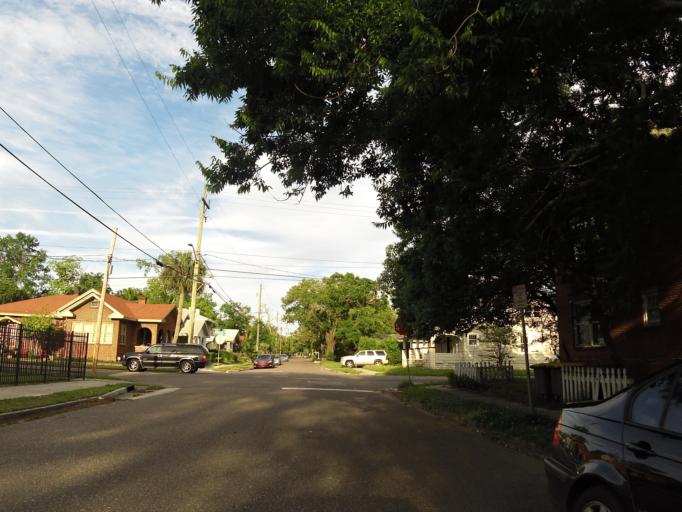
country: US
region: Florida
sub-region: Duval County
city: Jacksonville
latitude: 30.3542
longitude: -81.6616
